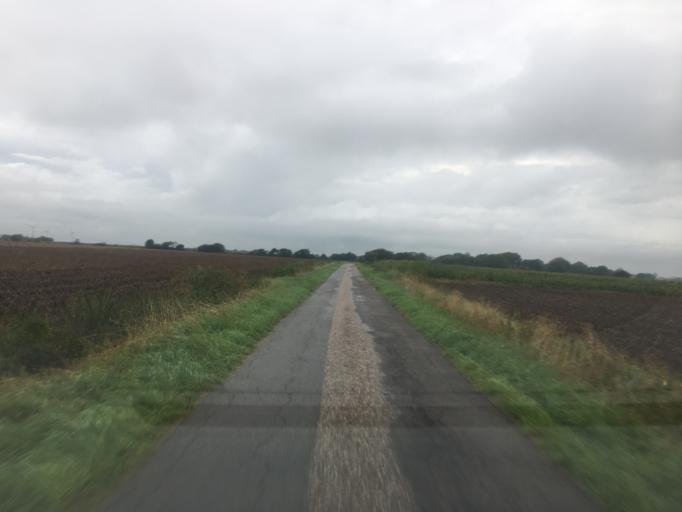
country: DK
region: South Denmark
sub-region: Tonder Kommune
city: Tonder
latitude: 54.9723
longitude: 8.9042
